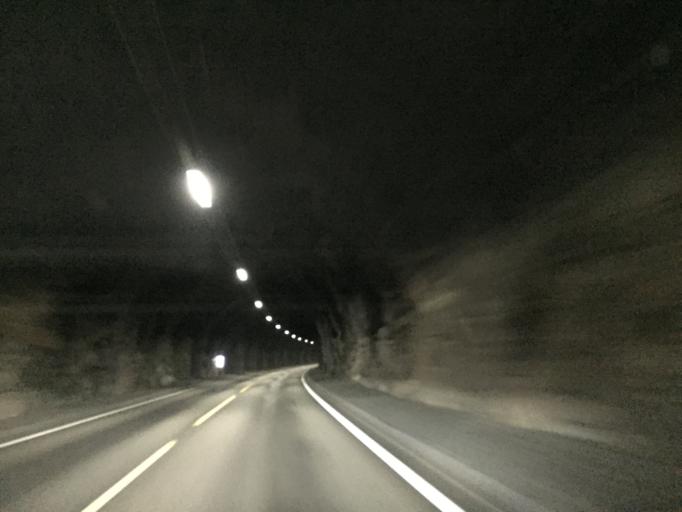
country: NO
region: Ostfold
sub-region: Hvaler
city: Skjaerhalden
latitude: 59.0373
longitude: 11.0025
